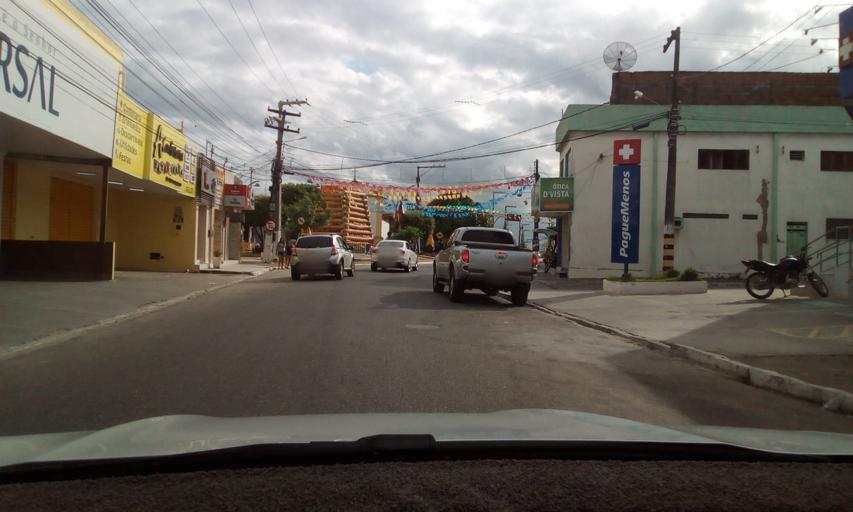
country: BR
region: Paraiba
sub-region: Mamanguape
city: Mamanguape
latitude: -6.8381
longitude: -35.1318
